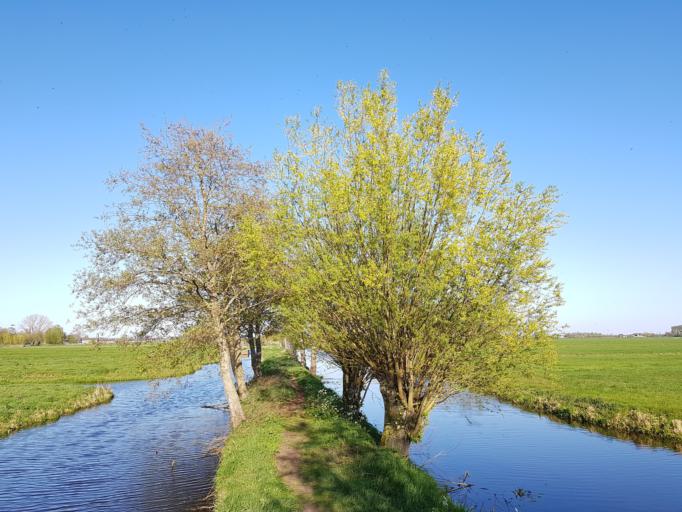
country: NL
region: South Holland
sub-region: Gemeente Vlist
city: Vlist
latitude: 52.0117
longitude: 4.8335
